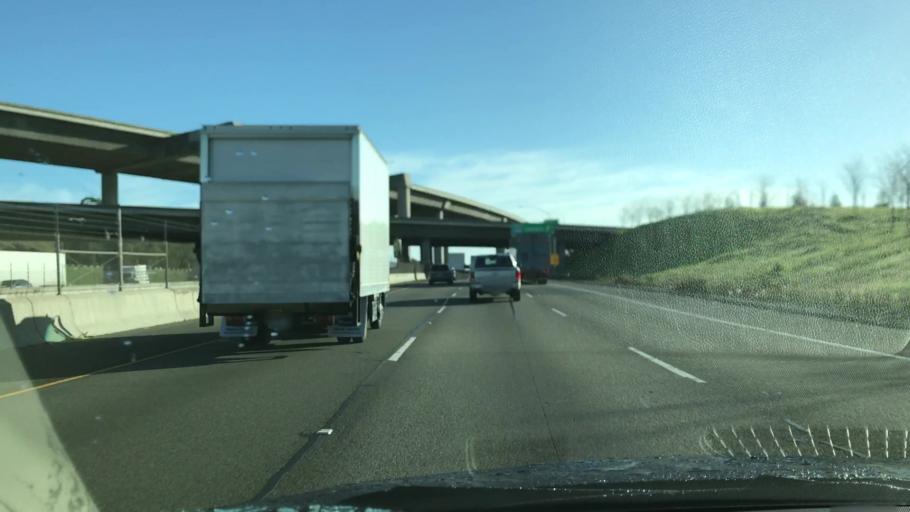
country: US
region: California
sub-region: Alameda County
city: Cherryland
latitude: 37.6897
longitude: -122.0994
